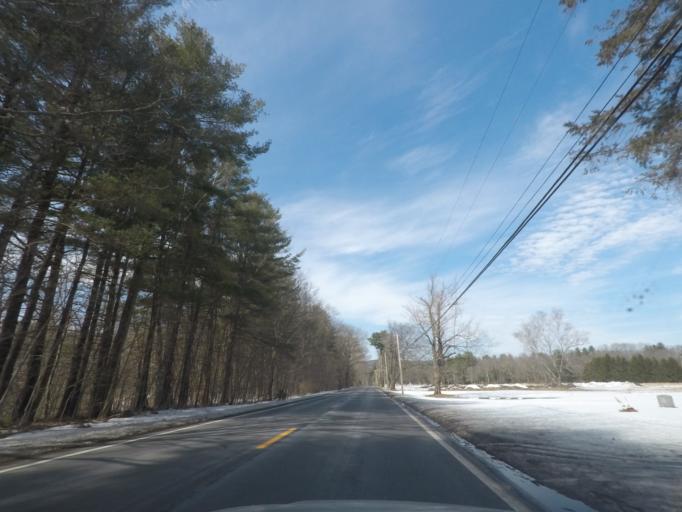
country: US
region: Massachusetts
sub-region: Berkshire County
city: West Stockbridge
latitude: 42.3474
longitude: -73.3810
